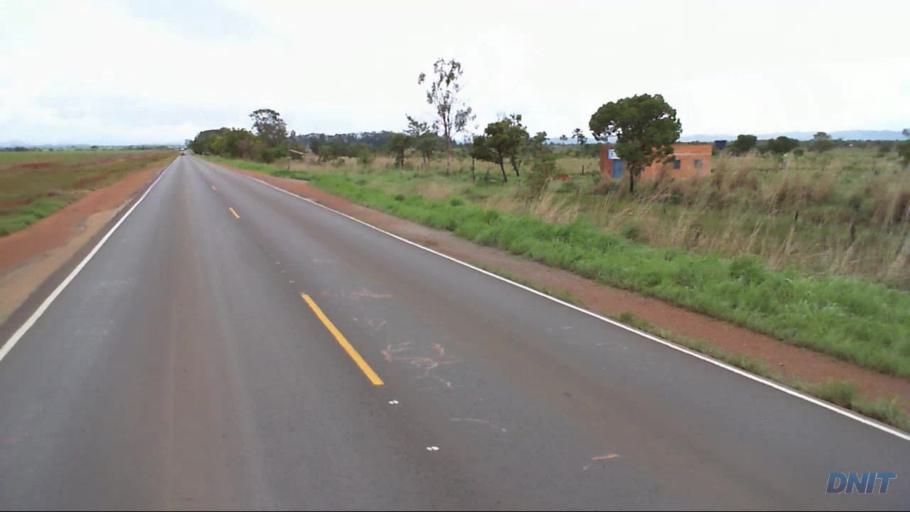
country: BR
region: Goias
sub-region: Padre Bernardo
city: Padre Bernardo
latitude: -15.3318
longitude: -48.2324
